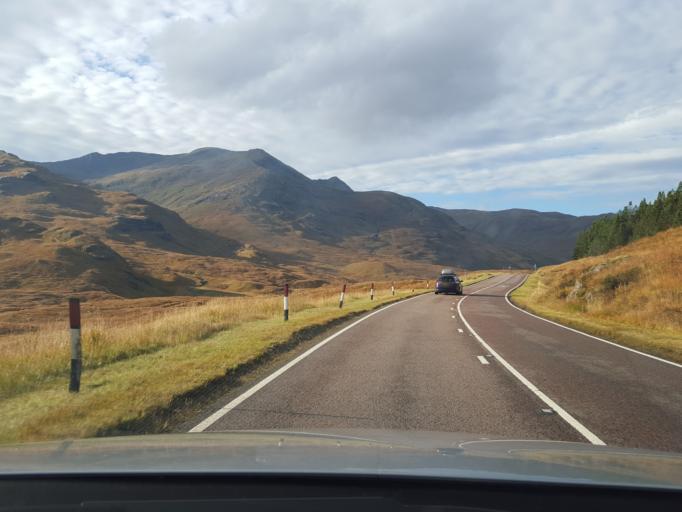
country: GB
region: Scotland
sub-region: Highland
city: Fort William
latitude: 57.1516
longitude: -5.2276
